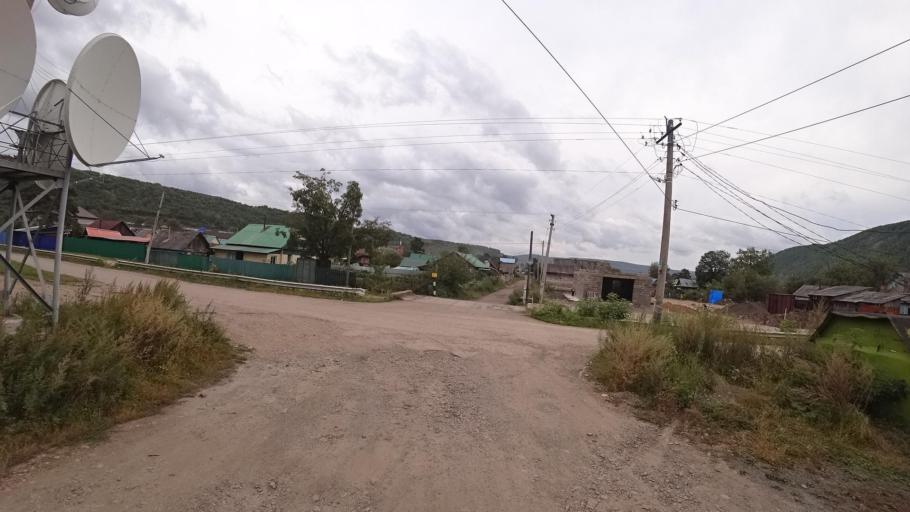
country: RU
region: Jewish Autonomous Oblast
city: Khingansk
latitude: 49.0086
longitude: 131.0507
